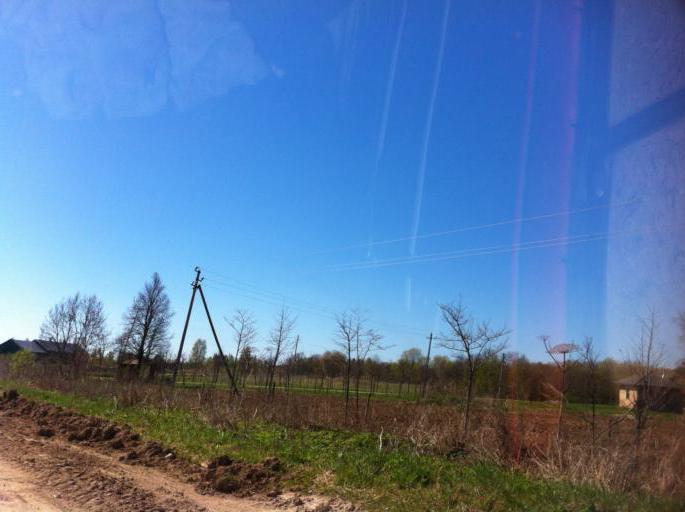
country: RU
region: Pskov
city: Izborsk
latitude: 57.8100
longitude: 27.9797
